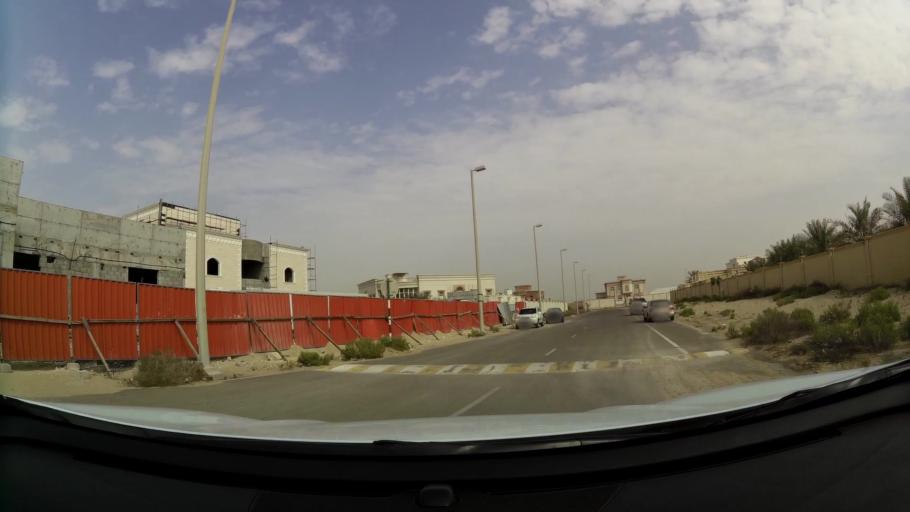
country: AE
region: Abu Dhabi
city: Abu Dhabi
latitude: 24.2743
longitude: 54.6634
